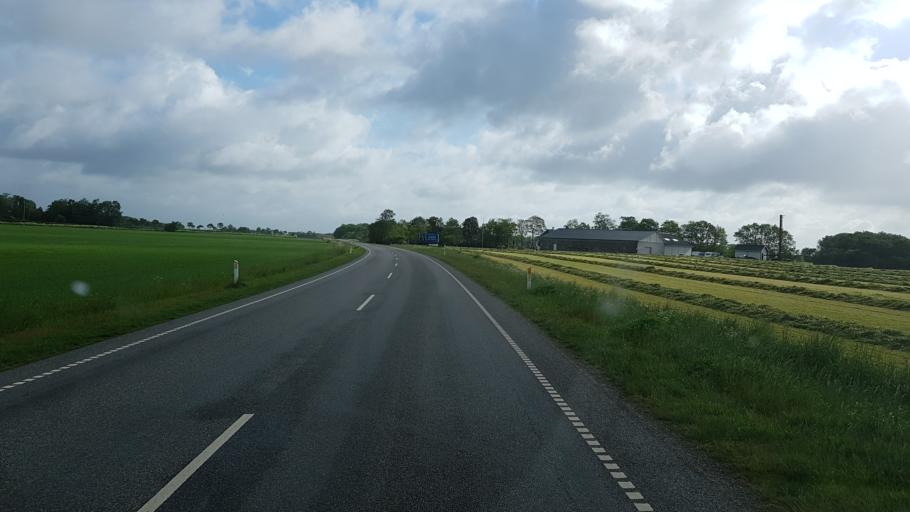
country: DK
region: South Denmark
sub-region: Vejen Kommune
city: Vejen
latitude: 55.4124
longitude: 9.1332
